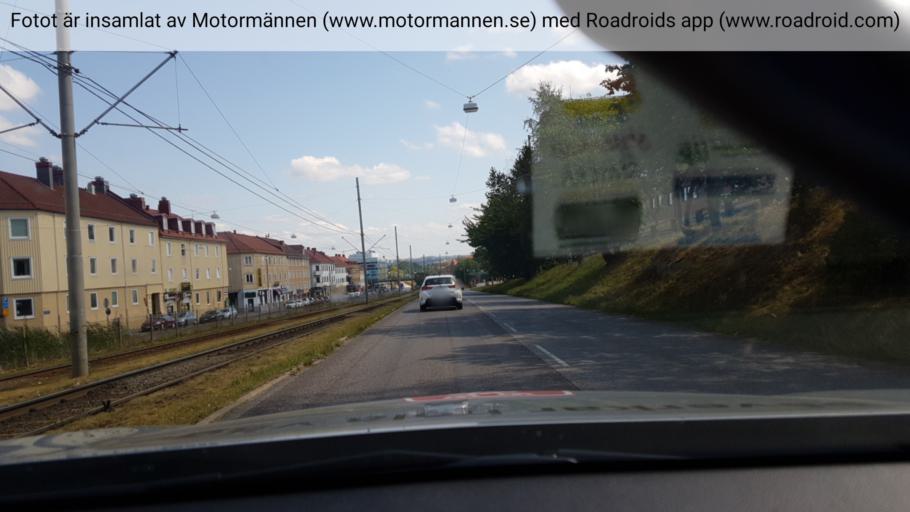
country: SE
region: Vaestra Goetaland
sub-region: Goteborg
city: Goeteborg
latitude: 57.7206
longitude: 11.9388
